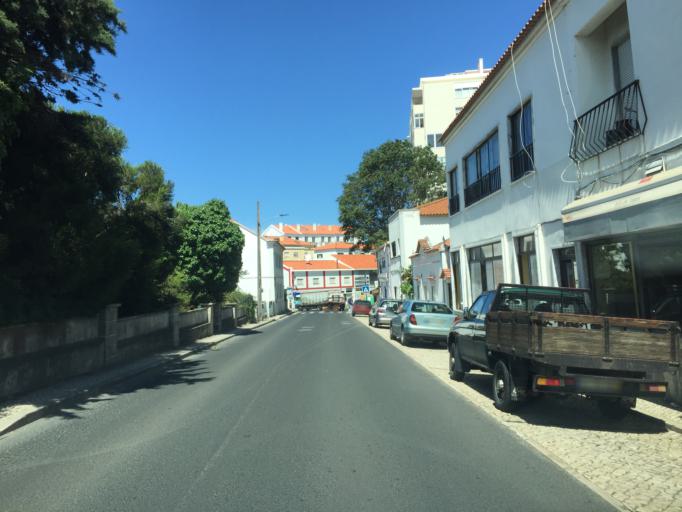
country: PT
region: Lisbon
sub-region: Lourinha
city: Lourinha
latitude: 39.2382
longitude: -9.3120
